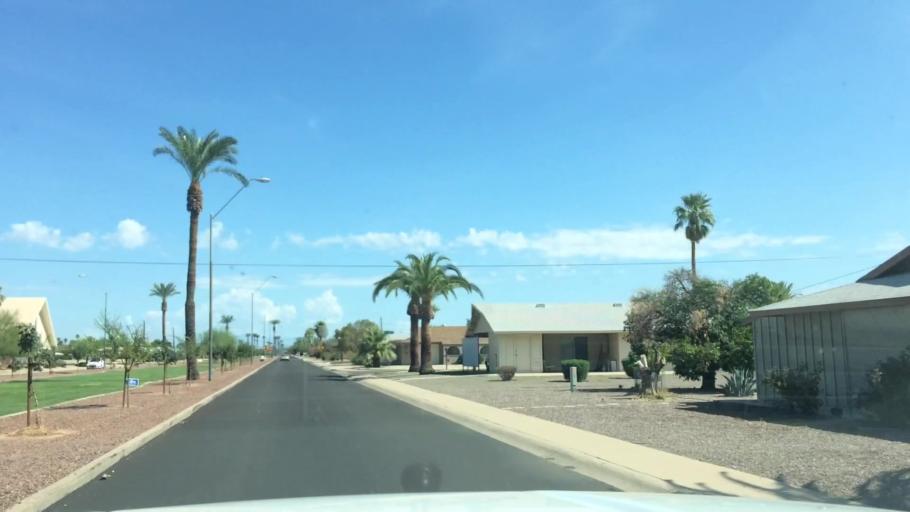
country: US
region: Arizona
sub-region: Maricopa County
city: Youngtown
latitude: 33.5854
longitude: -112.2899
